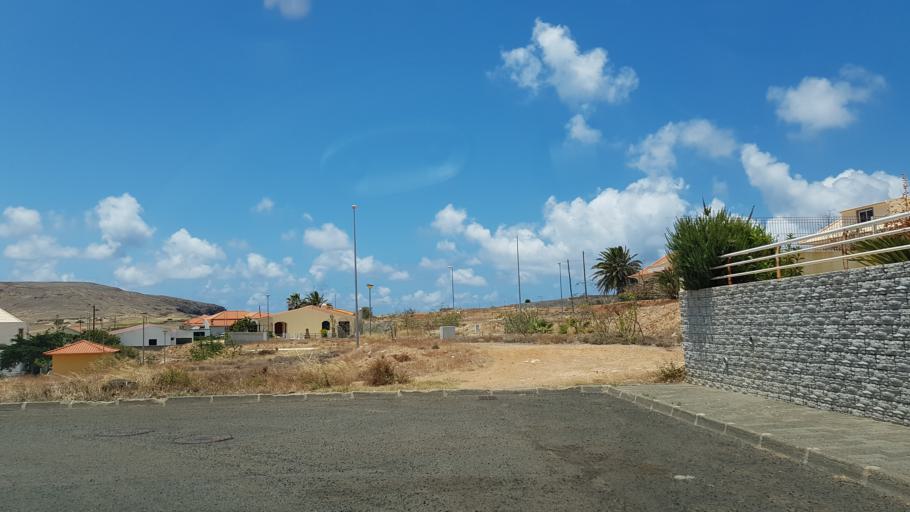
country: PT
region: Madeira
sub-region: Porto Santo
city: Vila de Porto Santo
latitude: 33.0562
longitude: -16.3648
